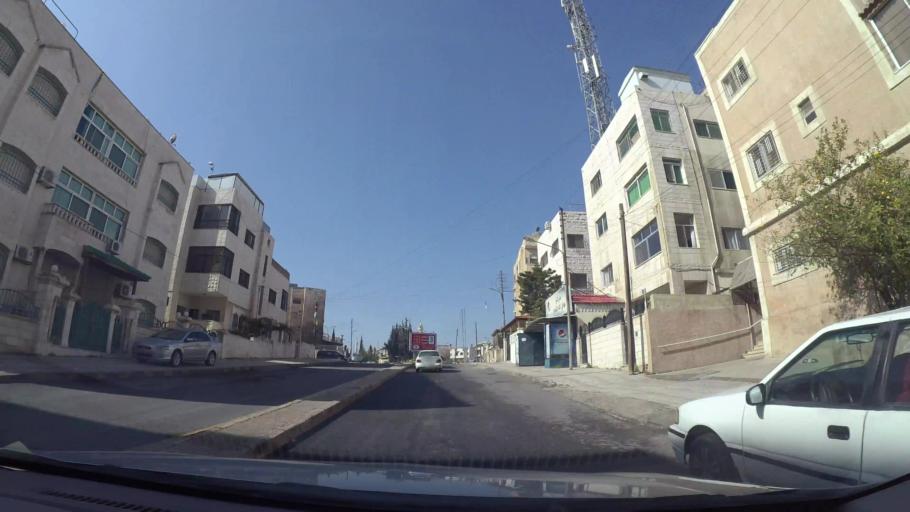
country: JO
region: Amman
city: Al Bunayyat ash Shamaliyah
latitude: 31.9310
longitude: 35.9052
